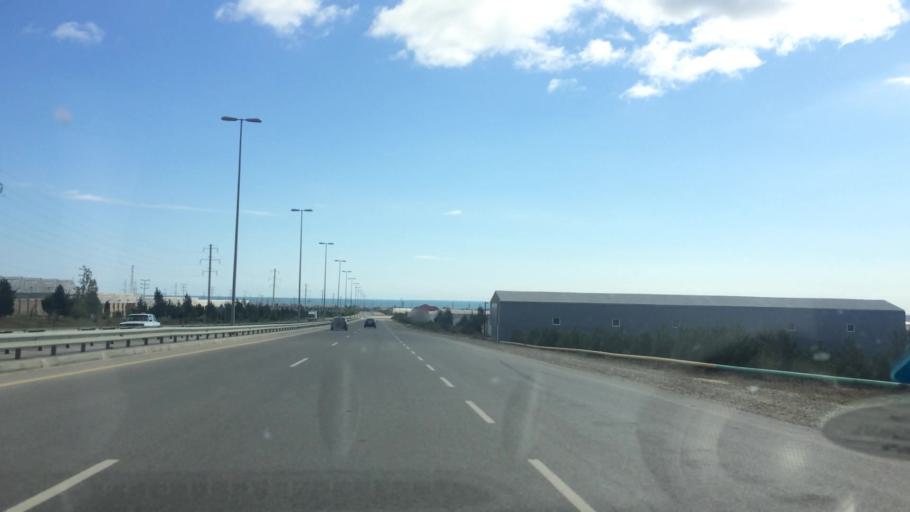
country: AZ
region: Baki
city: Zyrya
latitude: 40.4005
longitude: 50.3133
